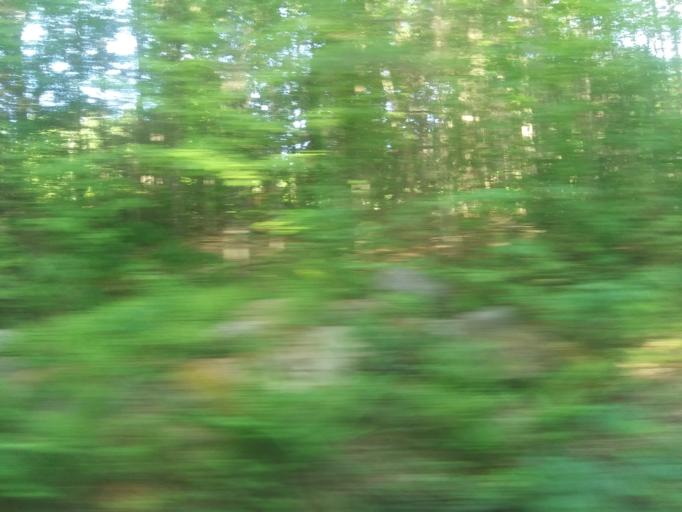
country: US
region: Massachusetts
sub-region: Franklin County
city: Shelburne Falls
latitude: 42.5915
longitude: -72.7459
